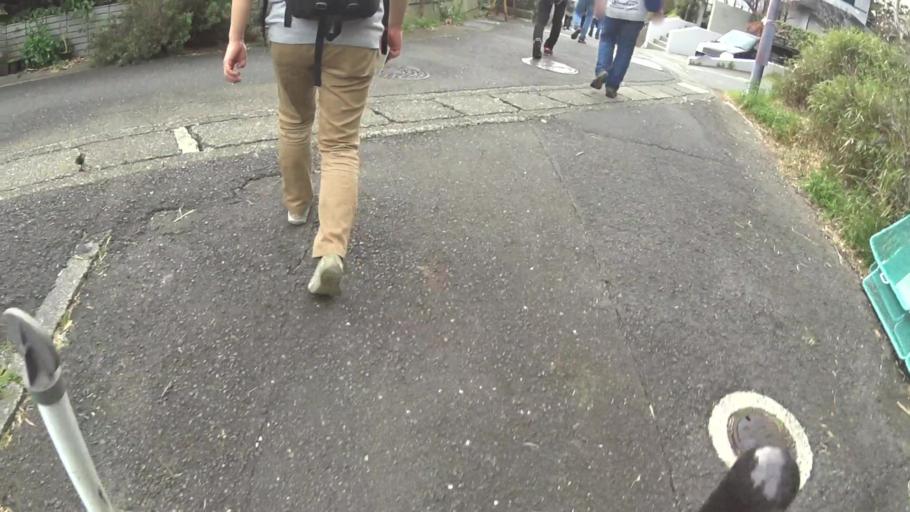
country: JP
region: Kanagawa
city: Kamakura
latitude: 35.3230
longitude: 139.5142
